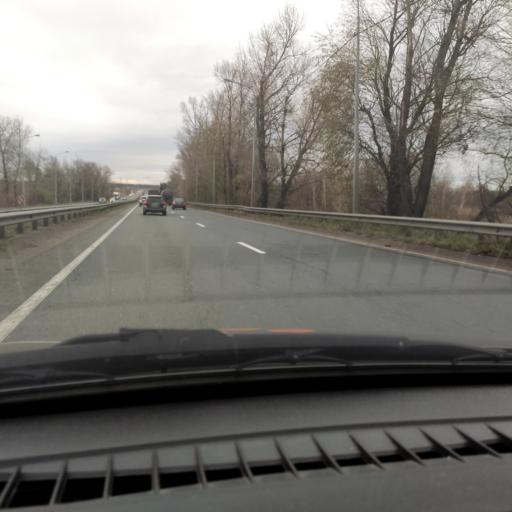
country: RU
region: Samara
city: Zhigulevsk
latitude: 53.5302
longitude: 49.5199
